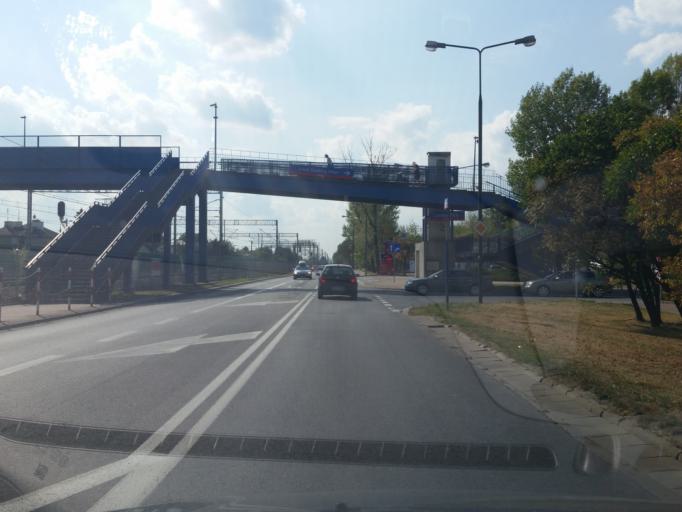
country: PL
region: Masovian Voivodeship
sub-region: Warszawa
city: Ursus
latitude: 52.2001
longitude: 20.8953
